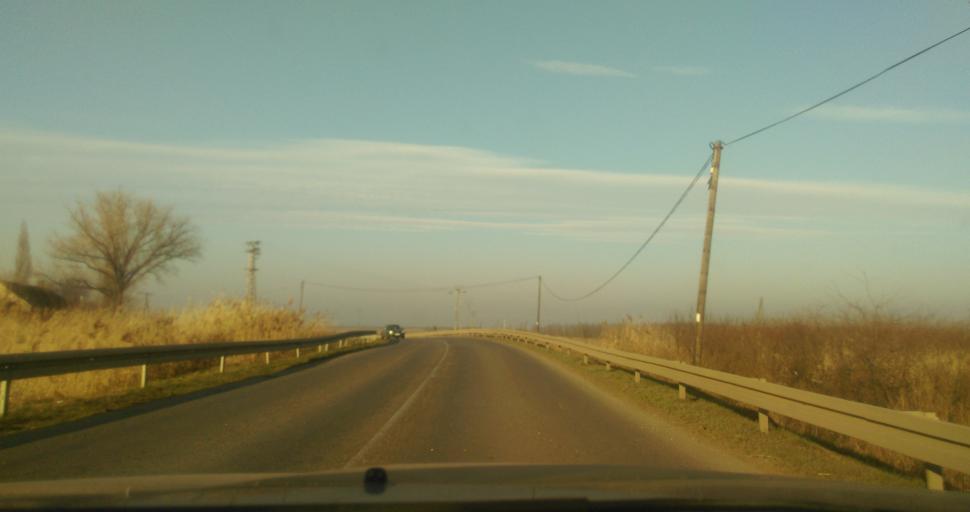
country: RS
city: Backo Gradiste
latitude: 45.5369
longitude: 20.0224
